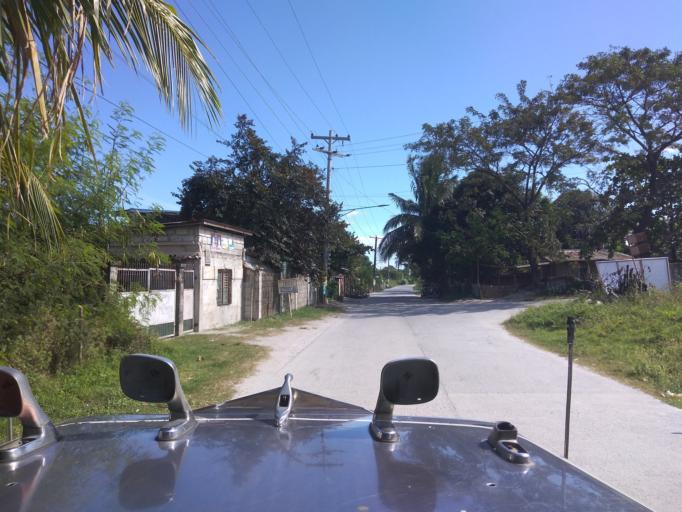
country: PH
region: Central Luzon
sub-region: Province of Pampanga
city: Magliman
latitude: 15.0278
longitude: 120.6359
